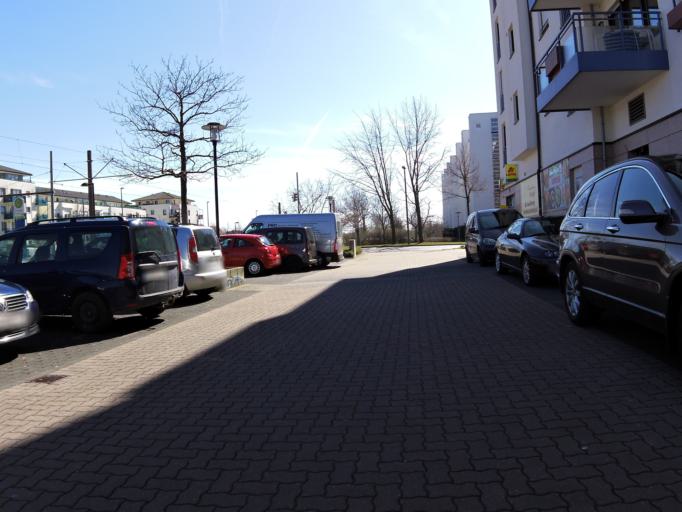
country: DE
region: Saxony
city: Taucha
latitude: 51.3590
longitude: 12.4730
